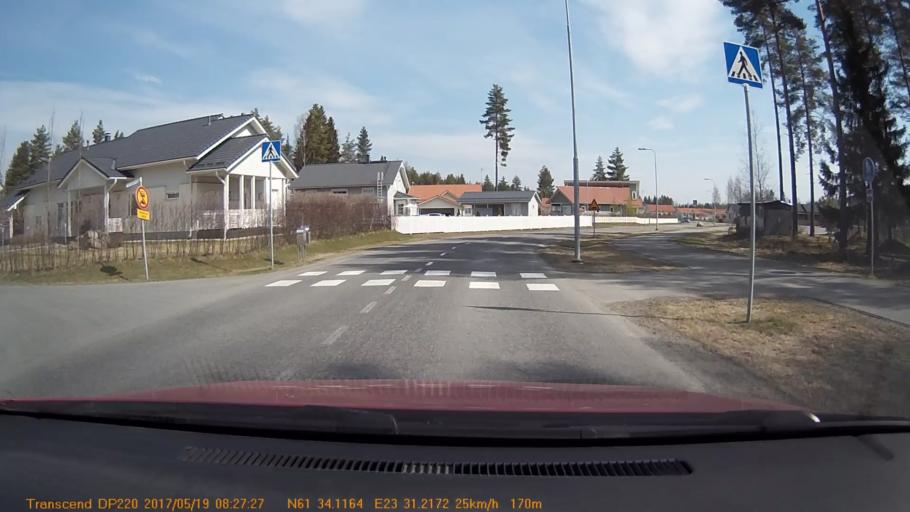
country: FI
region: Pirkanmaa
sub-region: Tampere
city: Yloejaervi
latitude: 61.5684
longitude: 23.5204
